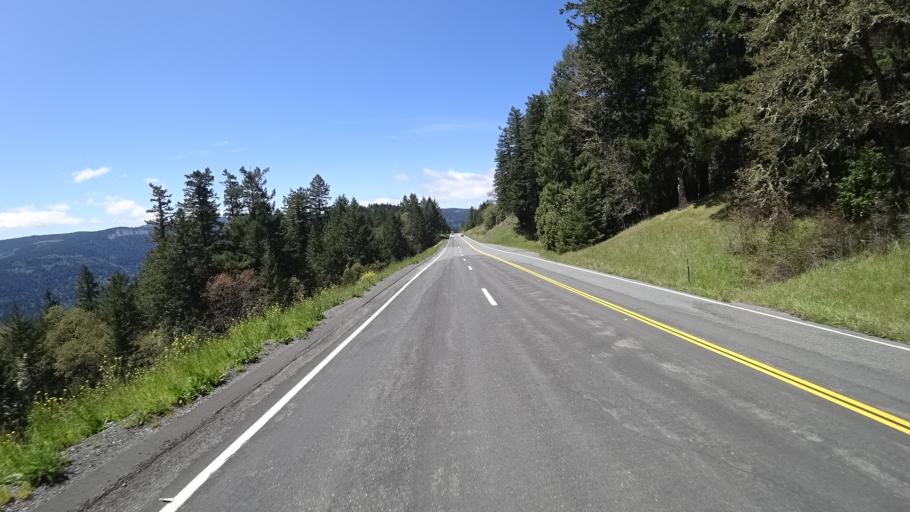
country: US
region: California
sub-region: Humboldt County
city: Willow Creek
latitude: 40.9259
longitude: -123.7995
